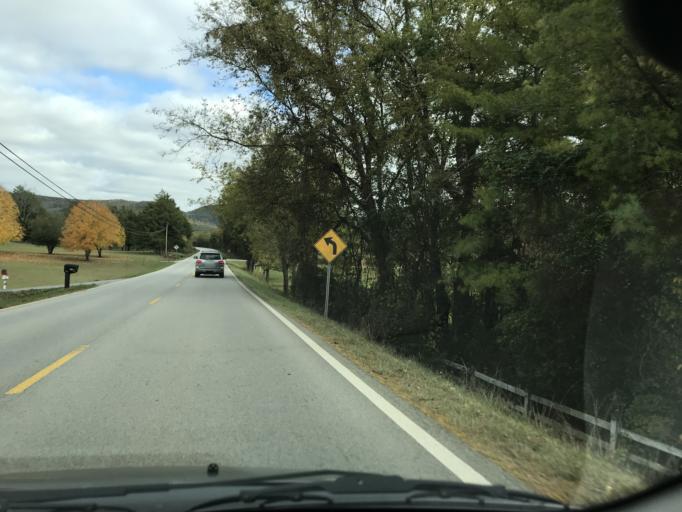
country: US
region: Tennessee
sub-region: Hamilton County
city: Lakesite
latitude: 35.1779
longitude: -85.0439
